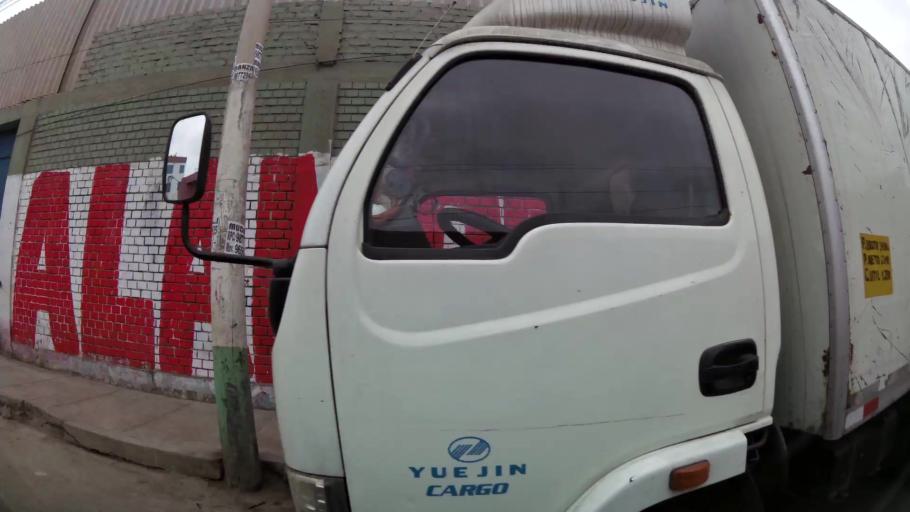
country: PE
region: Callao
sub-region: Callao
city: Callao
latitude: -12.0511
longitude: -77.1091
